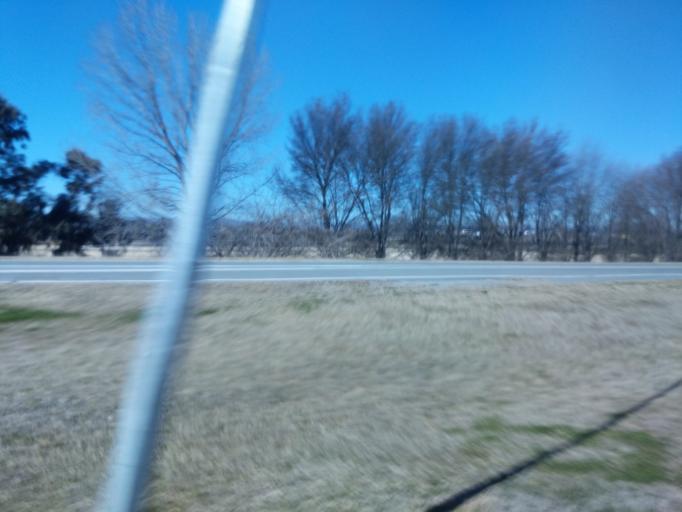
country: AU
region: Australian Capital Territory
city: Forrest
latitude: -35.3061
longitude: 149.1716
